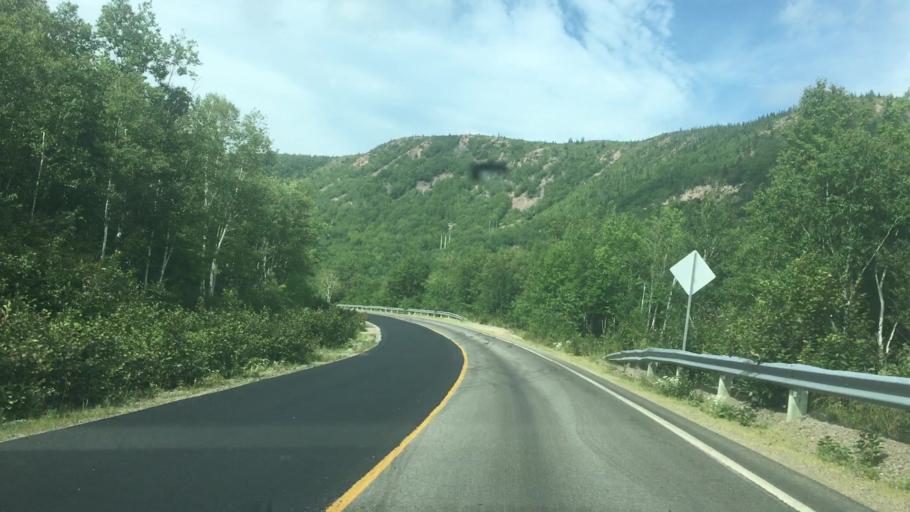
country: CA
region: Nova Scotia
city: Sydney Mines
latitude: 46.5780
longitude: -60.3891
